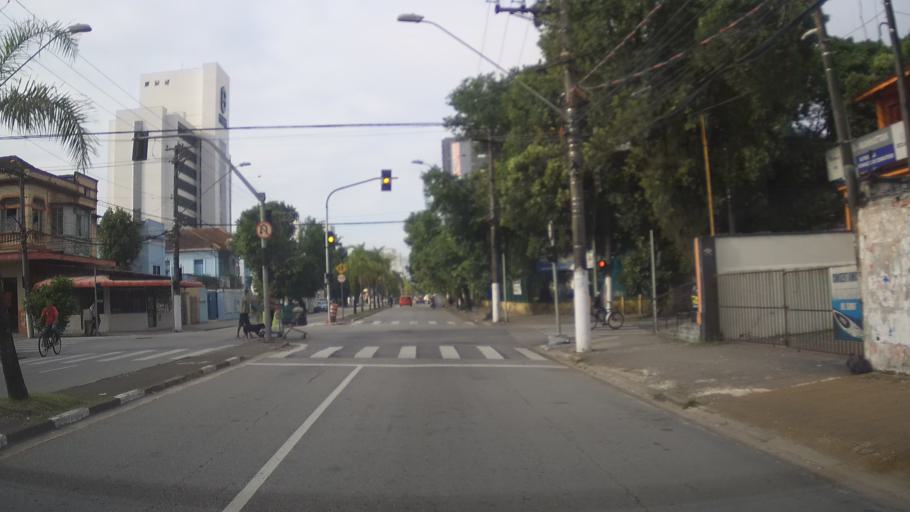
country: BR
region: Sao Paulo
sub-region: Santos
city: Santos
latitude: -23.9500
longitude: -46.3222
